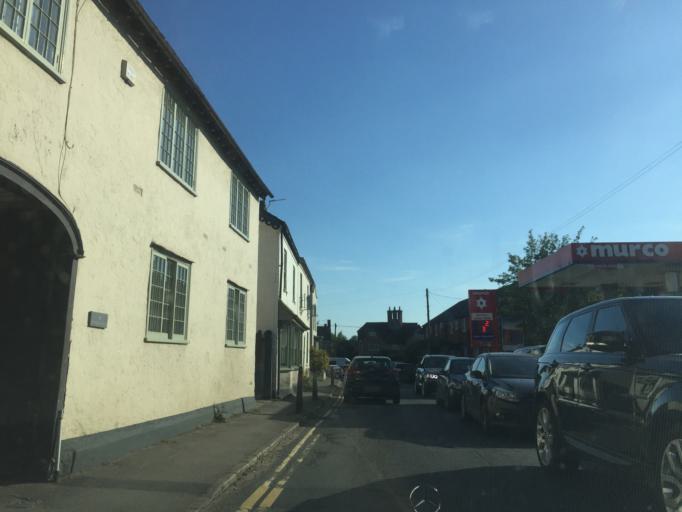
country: GB
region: England
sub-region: Oxfordshire
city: Watlington
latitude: 51.6441
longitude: -1.0058
